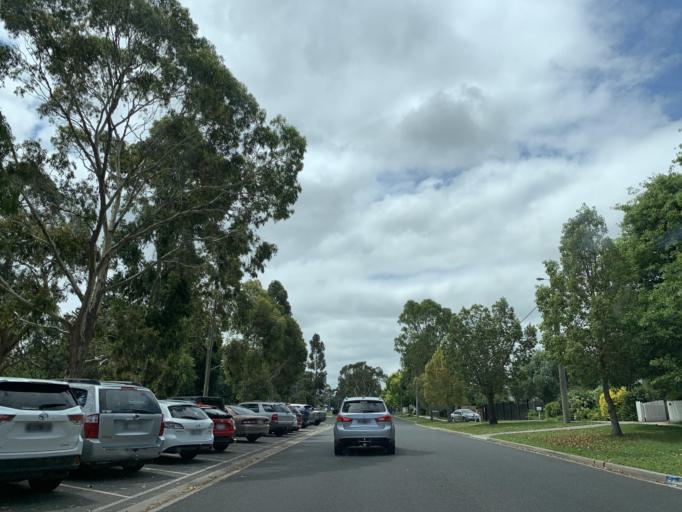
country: AU
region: Victoria
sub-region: Wellington
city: Sale
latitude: -38.1148
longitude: 147.0806
